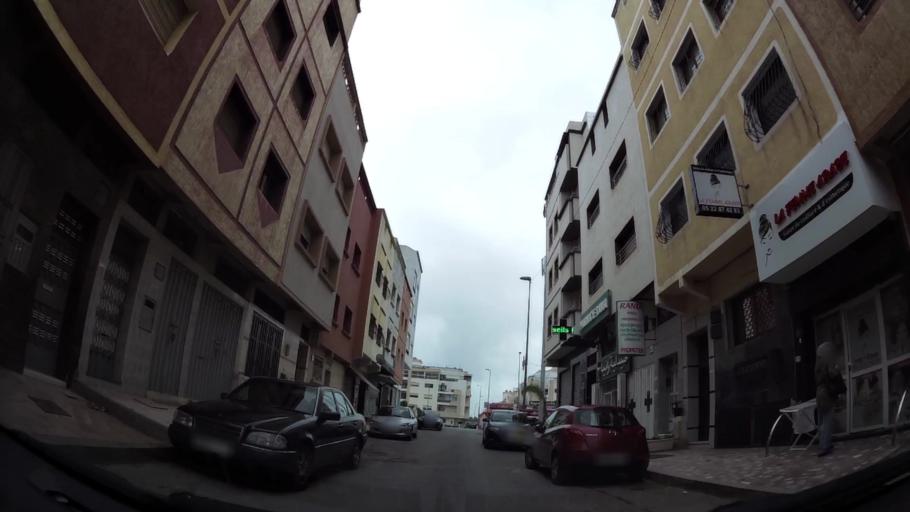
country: MA
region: Grand Casablanca
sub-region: Casablanca
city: Casablanca
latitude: 33.5308
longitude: -7.6121
